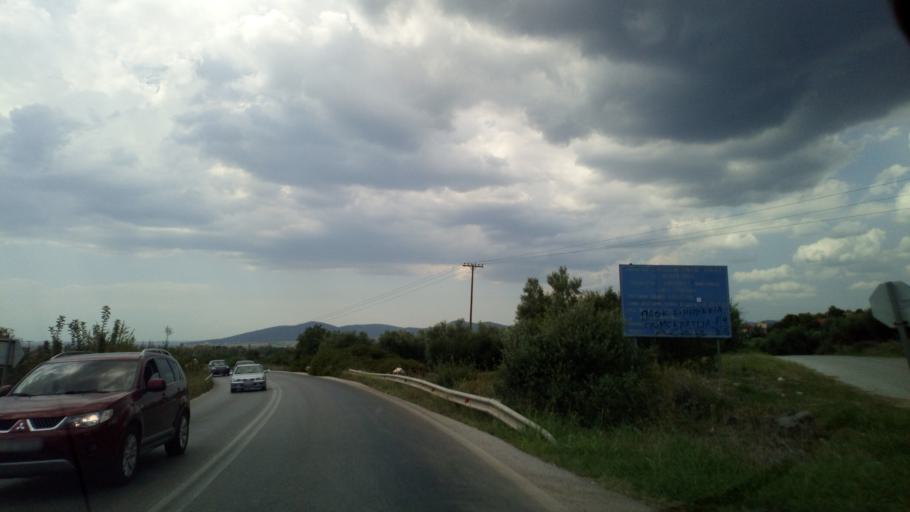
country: GR
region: Central Macedonia
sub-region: Nomos Chalkidikis
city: Ormylia
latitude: 40.2535
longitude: 23.5626
